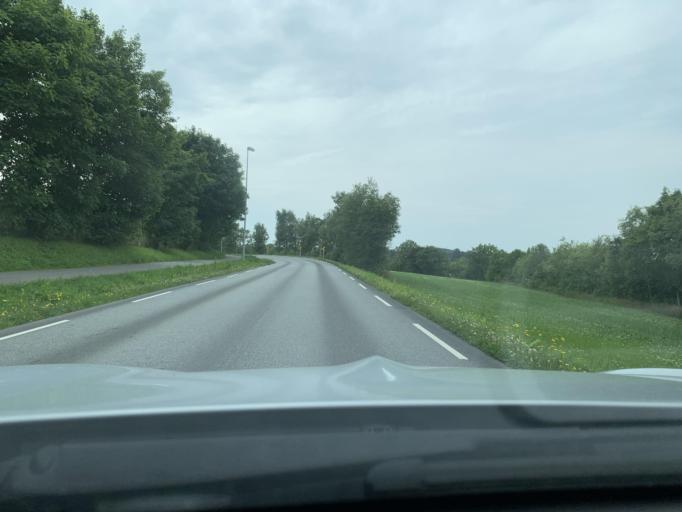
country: NO
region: Rogaland
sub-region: Time
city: Bryne
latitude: 58.7703
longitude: 5.7223
